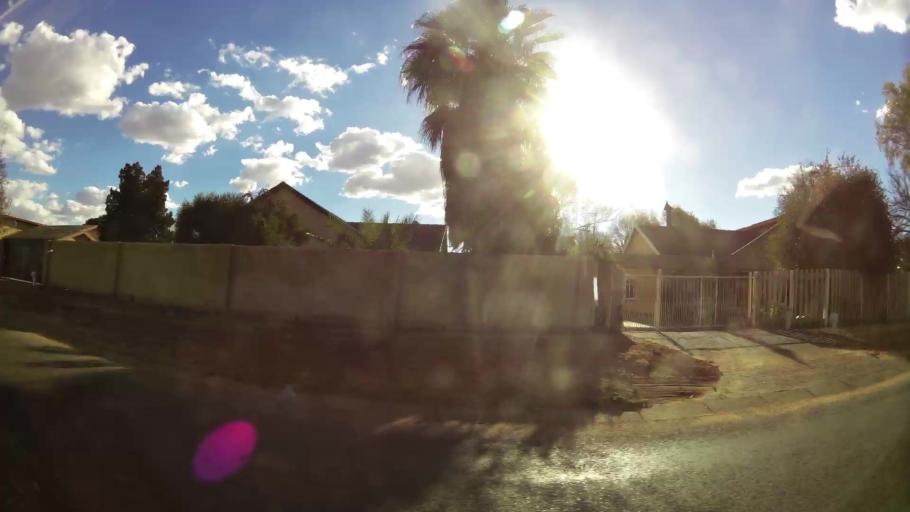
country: ZA
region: North-West
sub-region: Dr Kenneth Kaunda District Municipality
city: Klerksdorp
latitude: -26.8365
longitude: 26.6600
